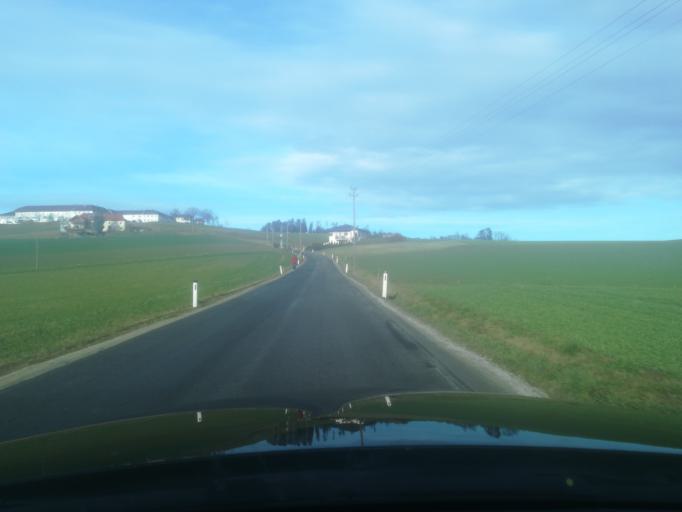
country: AT
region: Upper Austria
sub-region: Politischer Bezirk Perg
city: Perg
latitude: 48.3422
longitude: 14.6211
